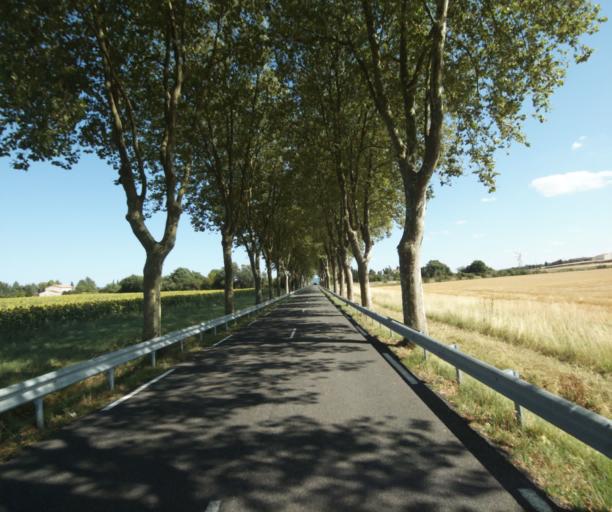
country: FR
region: Midi-Pyrenees
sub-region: Departement de la Haute-Garonne
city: Saint-Felix-Lauragais
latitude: 43.4841
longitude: 1.9122
